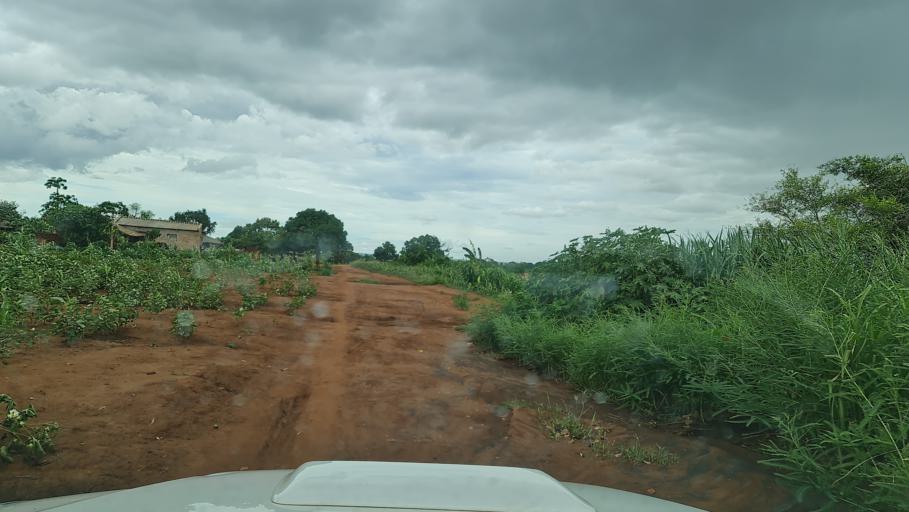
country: MZ
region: Nampula
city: Nacala
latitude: -14.7490
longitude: 40.0255
